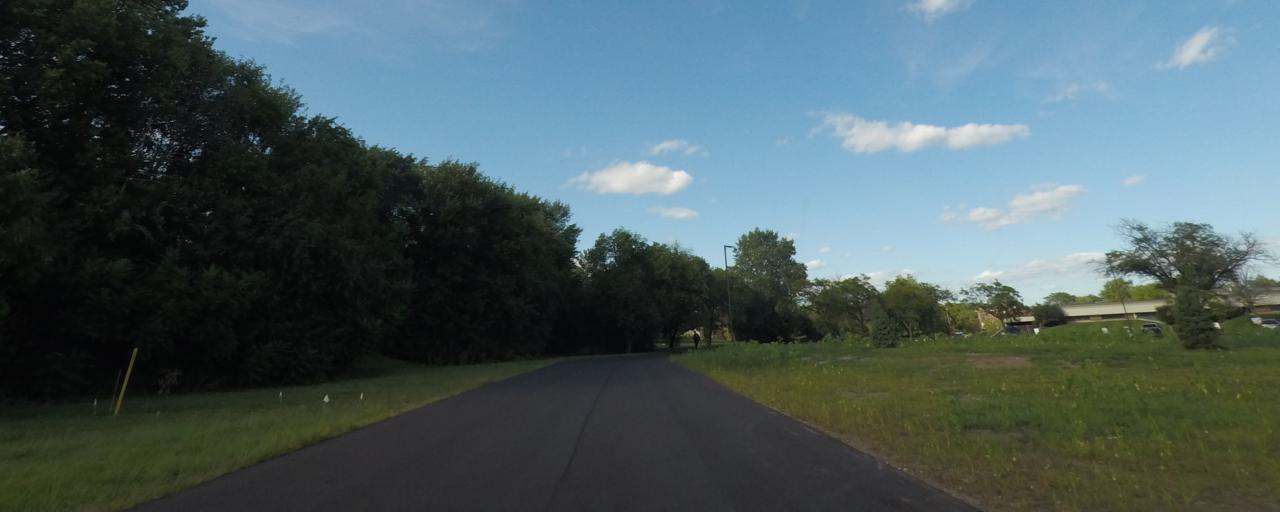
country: US
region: Wisconsin
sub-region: Dane County
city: Middleton
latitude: 43.0631
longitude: -89.5052
